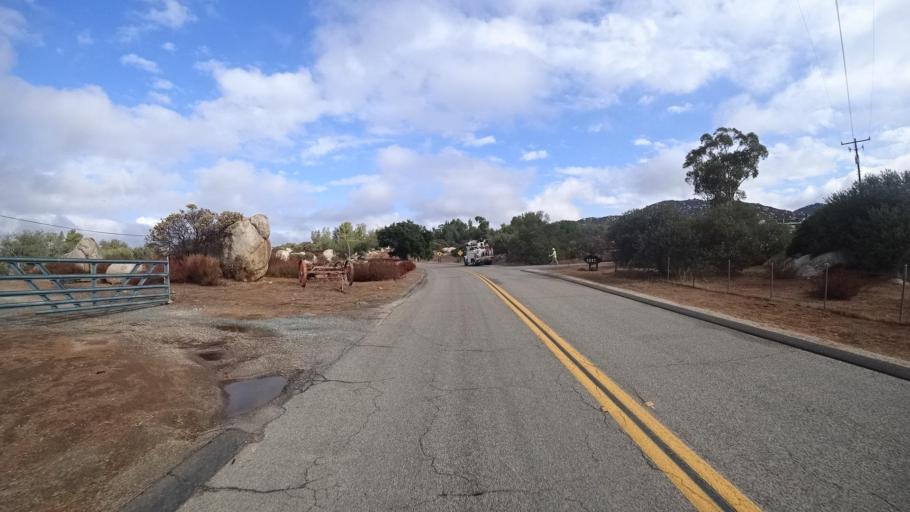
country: MX
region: Baja California
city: Tecate
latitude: 32.6332
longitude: -116.6350
